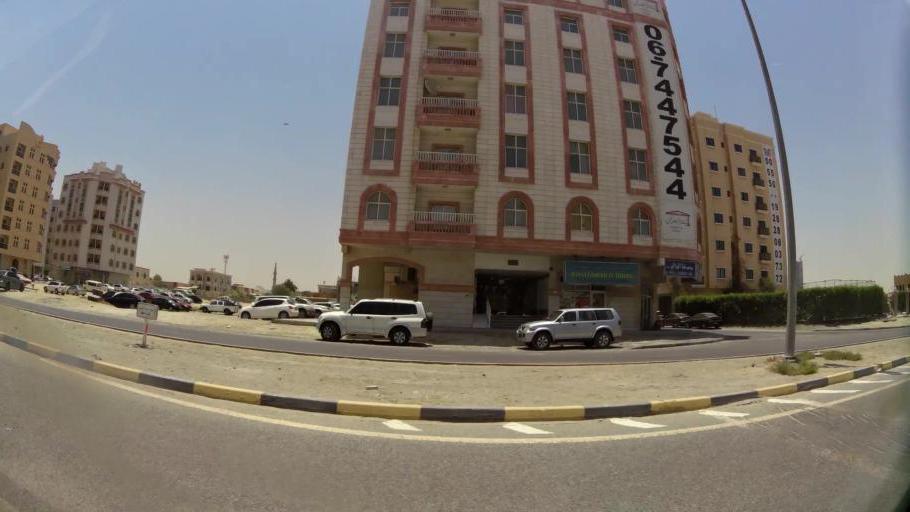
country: AE
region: Ajman
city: Ajman
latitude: 25.4072
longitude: 55.5126
